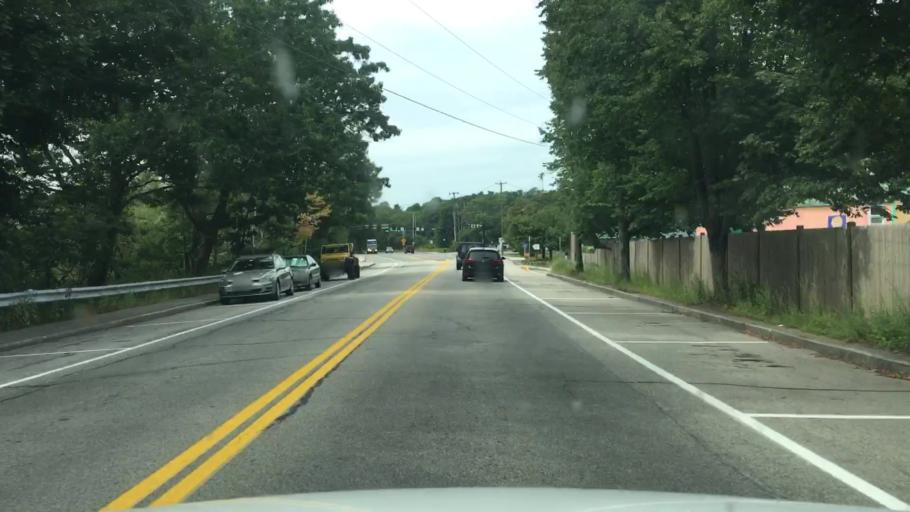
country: US
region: Maine
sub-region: York County
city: Kittery
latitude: 43.0870
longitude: -70.7471
